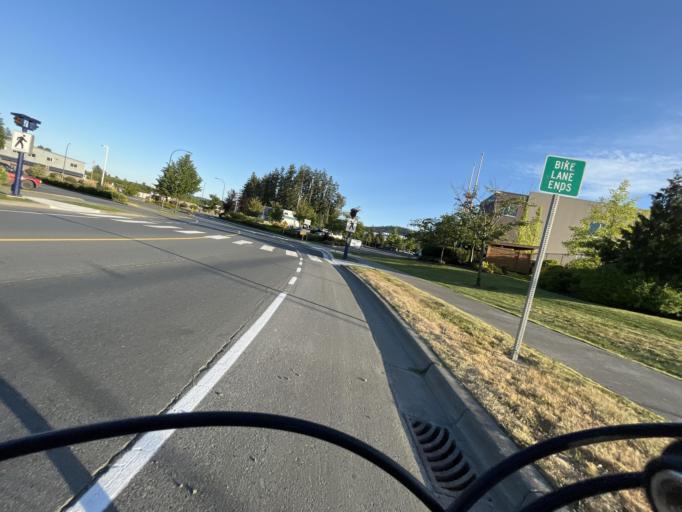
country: CA
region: British Columbia
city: Langford
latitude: 48.4569
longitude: -123.5407
